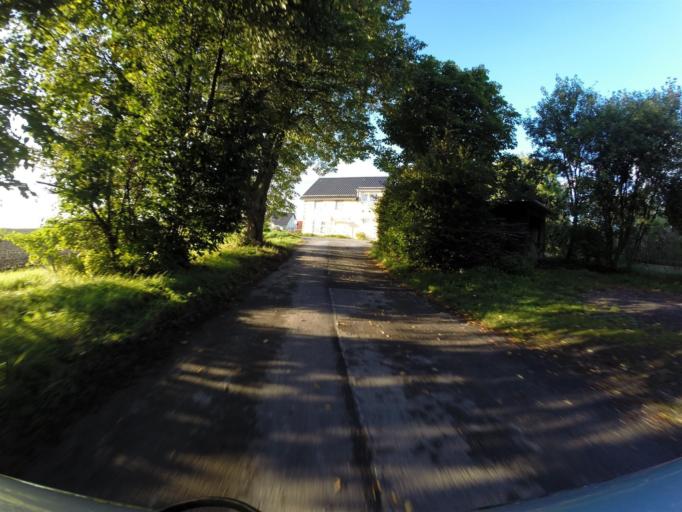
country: DE
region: Thuringia
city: Bucha
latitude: 50.8822
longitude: 11.5096
